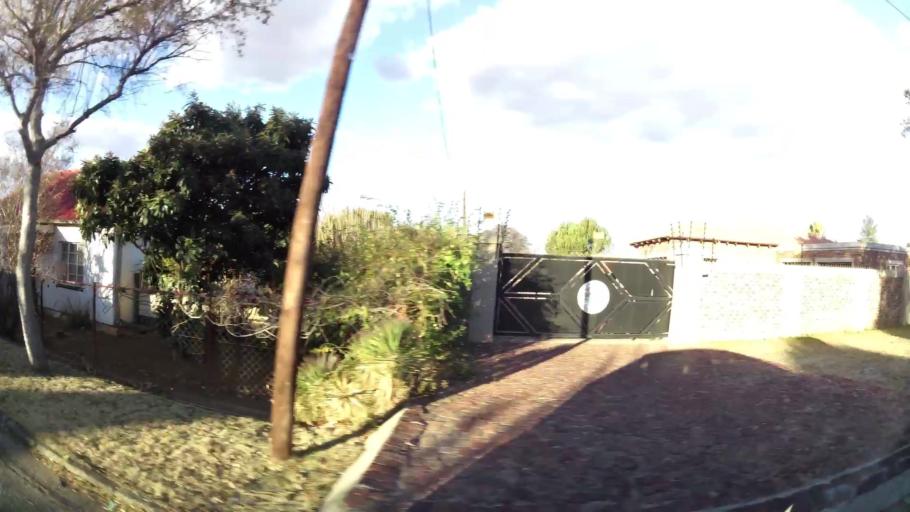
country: ZA
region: North-West
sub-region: Dr Kenneth Kaunda District Municipality
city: Potchefstroom
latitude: -26.7302
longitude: 27.0998
